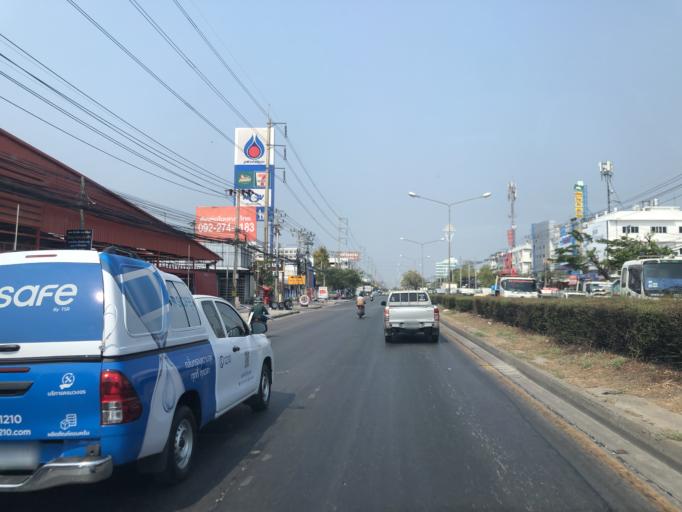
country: TH
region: Bangkok
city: Bang Na
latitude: 13.6058
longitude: 100.6927
